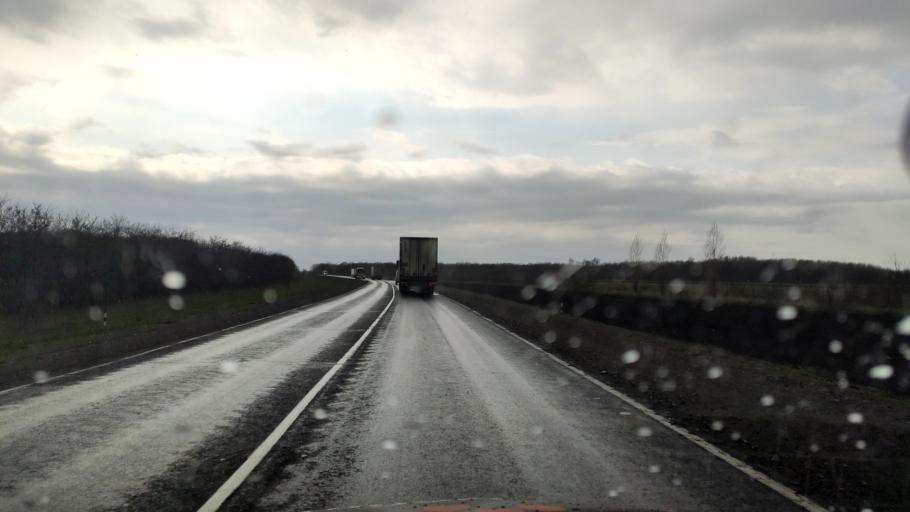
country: RU
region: Voronezj
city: Nizhnedevitsk
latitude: 51.5765
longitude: 38.3104
